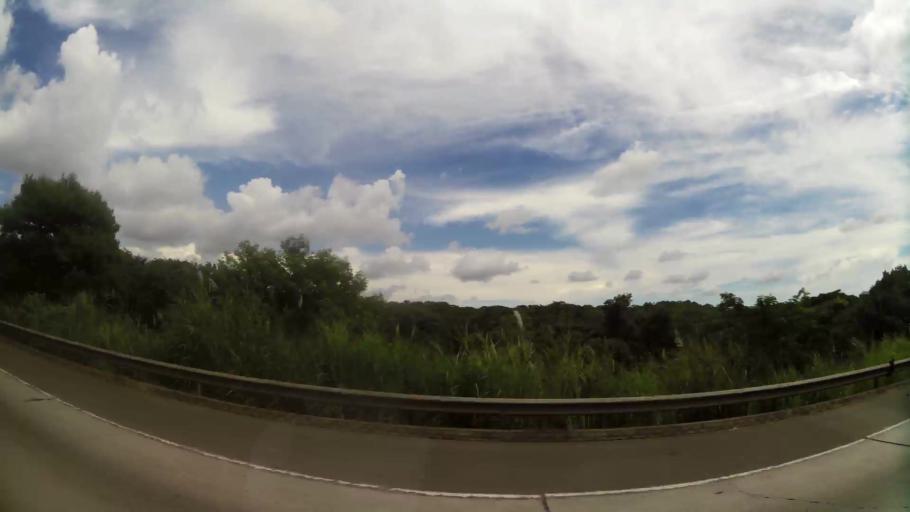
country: PA
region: Panama
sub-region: Distrito Arraijan
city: Arraijan
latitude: 8.9862
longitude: -79.6481
